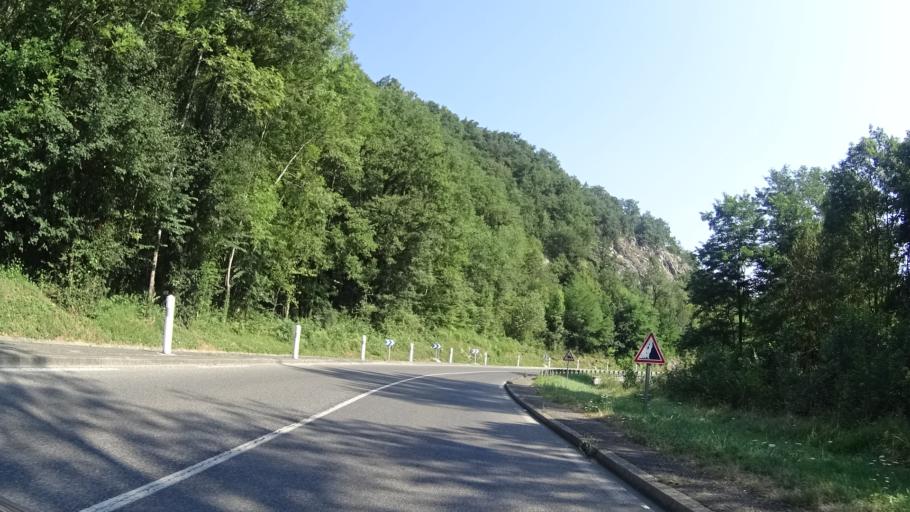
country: FR
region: Midi-Pyrenees
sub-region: Departement de l'Ariege
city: Lavelanet
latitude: 42.9553
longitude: 1.8609
